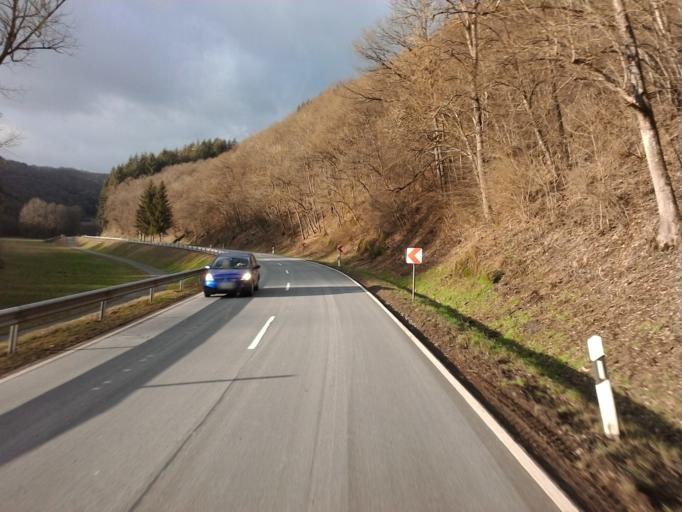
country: DE
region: Rheinland-Pfalz
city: Niederraden
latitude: 49.9875
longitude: 6.3143
